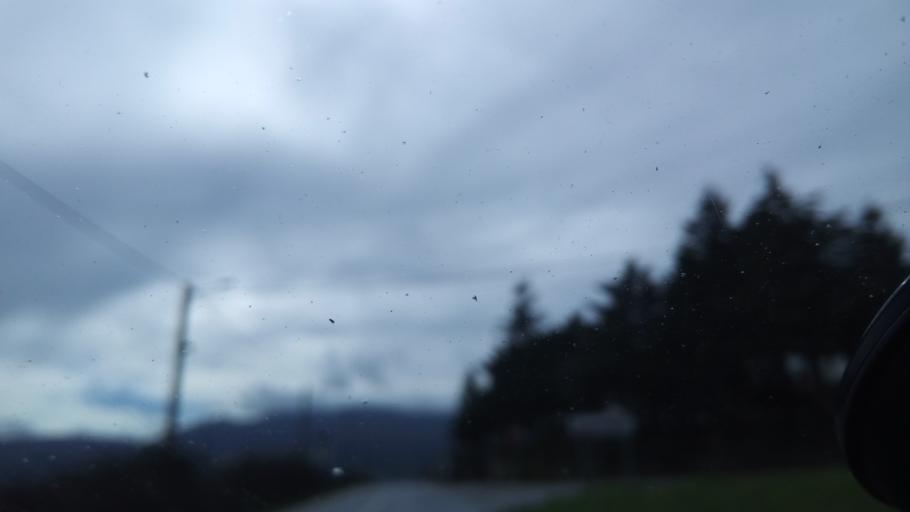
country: PT
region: Guarda
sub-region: Fornos de Algodres
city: Fornos de Algodres
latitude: 40.5540
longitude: -7.5696
